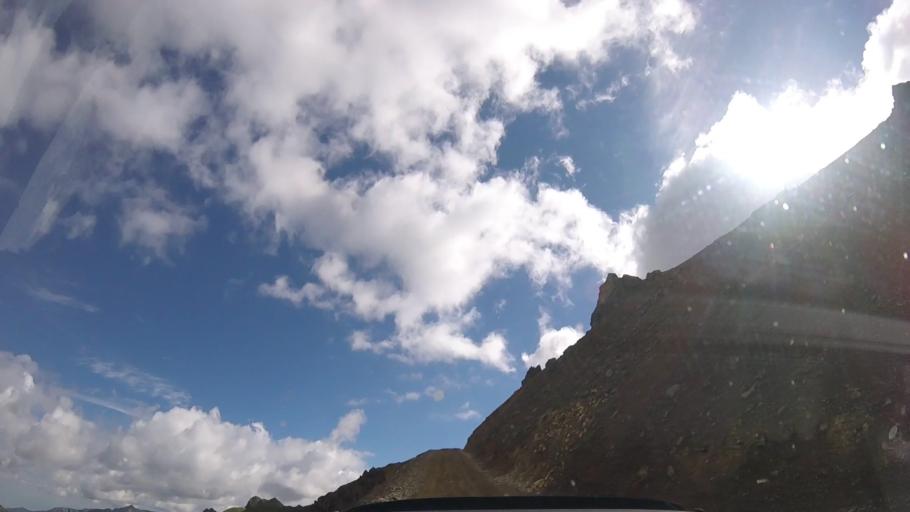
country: US
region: Colorado
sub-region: San Juan County
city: Silverton
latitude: 37.9169
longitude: -107.6186
